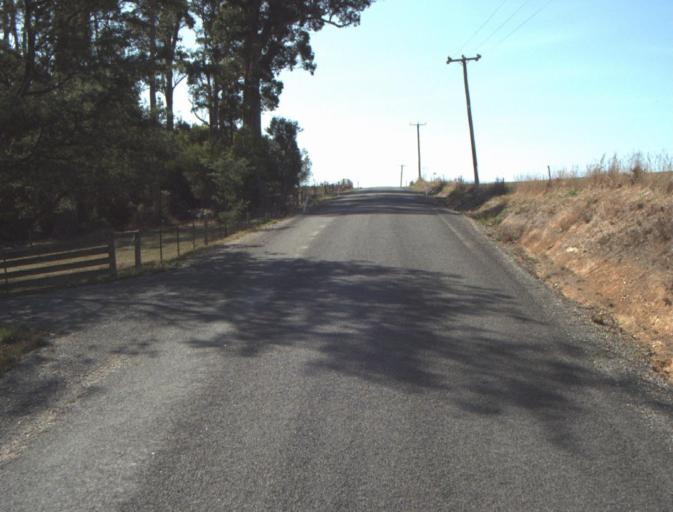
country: AU
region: Tasmania
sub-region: Launceston
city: Mayfield
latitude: -41.2344
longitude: 147.2346
